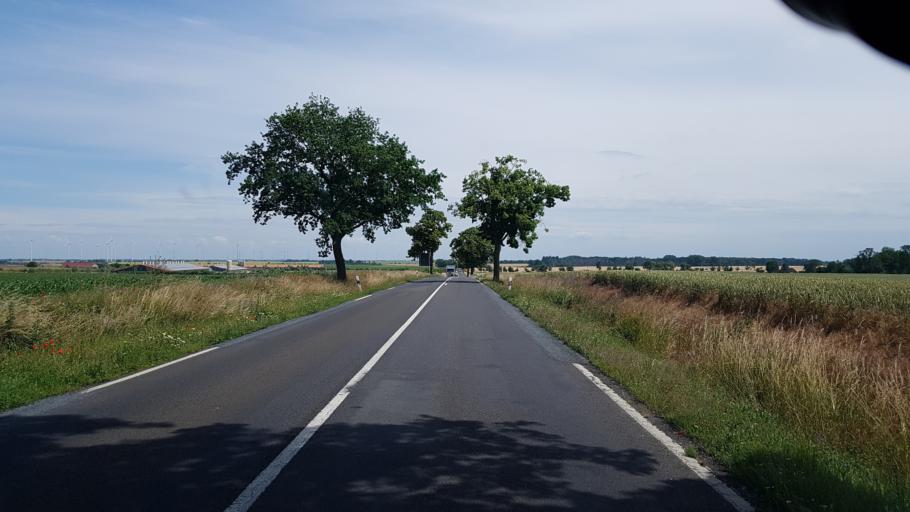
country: DE
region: Mecklenburg-Vorpommern
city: Strasburg
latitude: 53.4041
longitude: 13.7450
